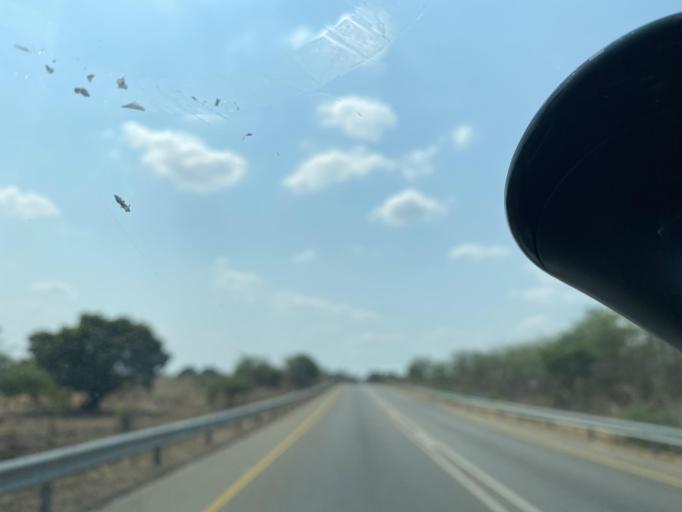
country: ZM
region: Lusaka
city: Chongwe
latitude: -15.5547
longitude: 28.6810
